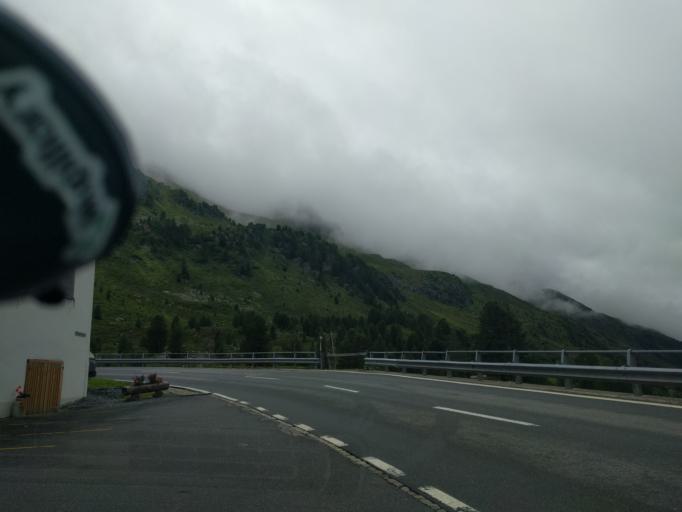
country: CH
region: Grisons
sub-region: Praettigau/Davos District
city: Davos
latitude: 46.7869
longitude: 9.9191
